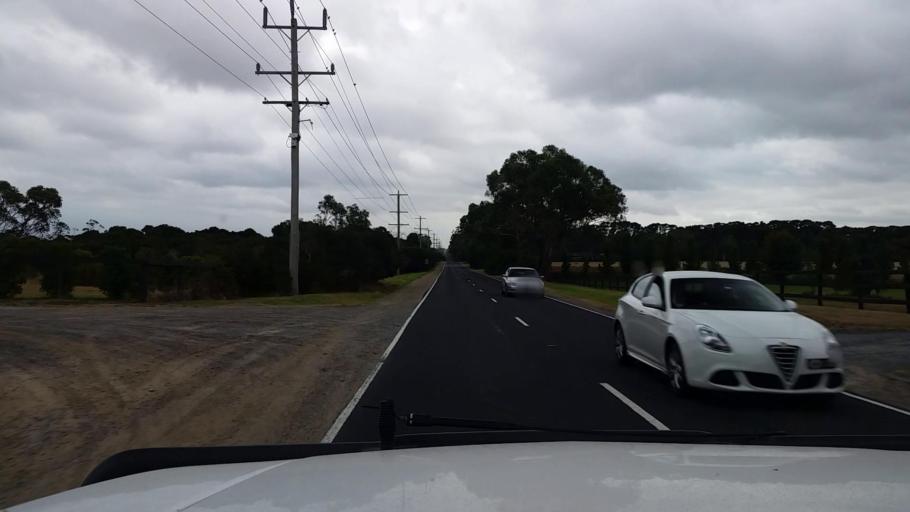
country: AU
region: Victoria
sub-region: Mornington Peninsula
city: Somerville
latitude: -38.2152
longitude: 145.1562
